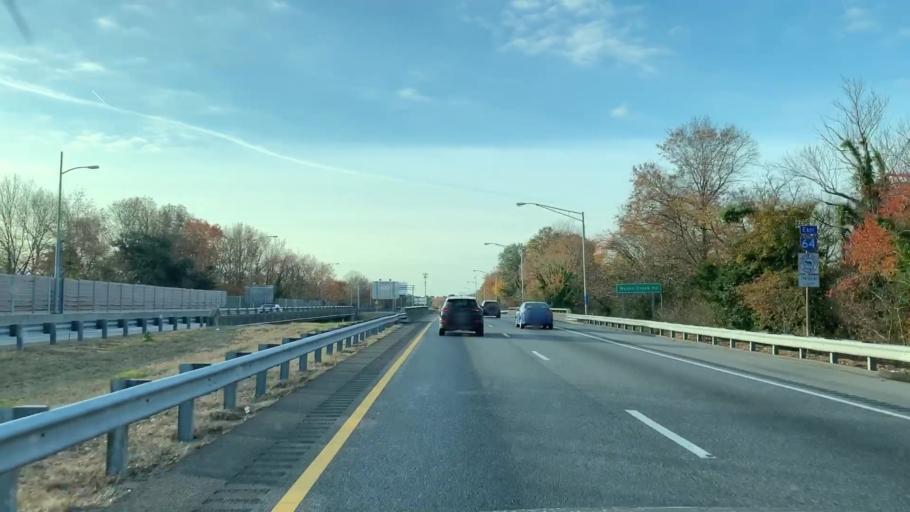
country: US
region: Virginia
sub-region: City of Norfolk
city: Norfolk
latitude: 36.9505
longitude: -76.2655
